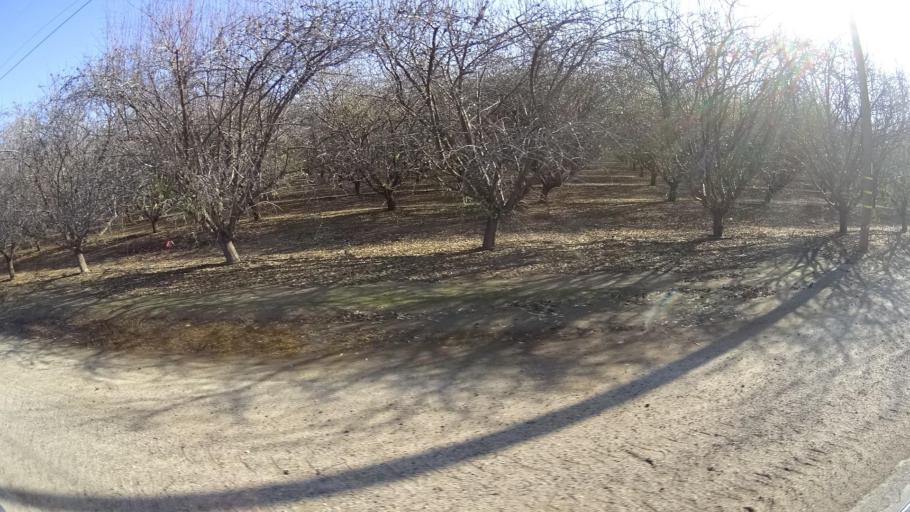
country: US
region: California
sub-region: Kern County
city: Weedpatch
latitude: 35.2037
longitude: -118.8961
